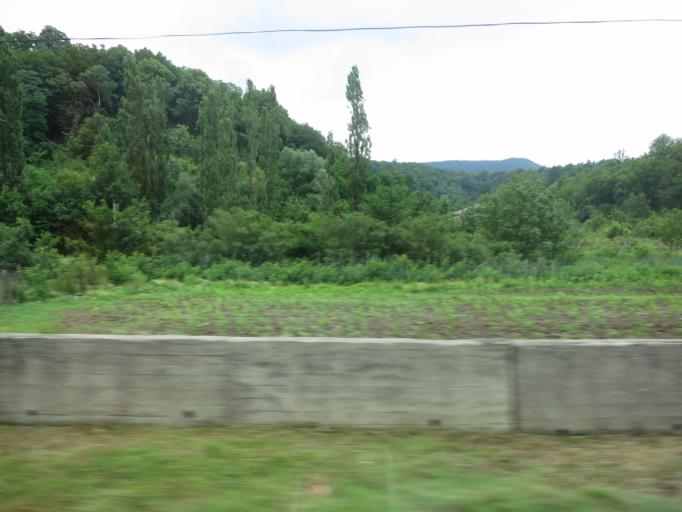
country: GE
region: Samegrelo and Zemo Svaneti
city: Abasha
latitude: 42.0957
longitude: 42.2109
